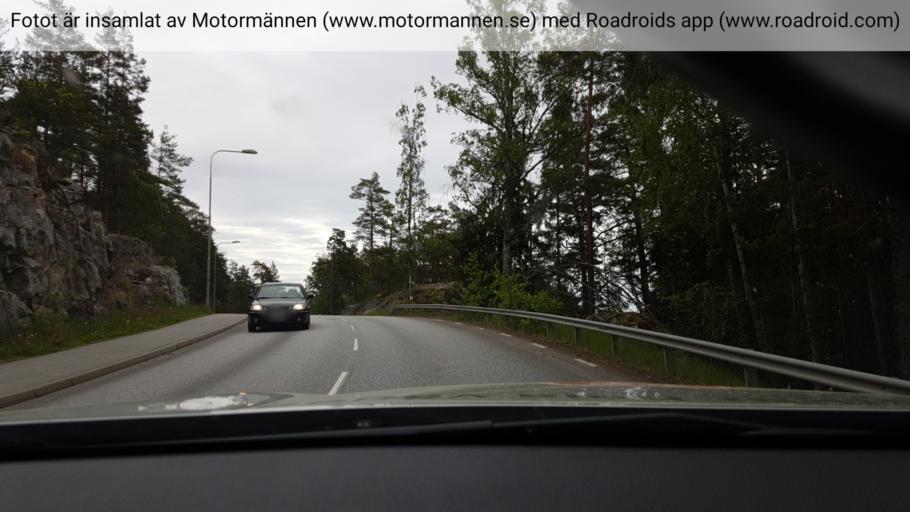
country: SE
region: Stockholm
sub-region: Nacka Kommun
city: Saltsjobaden
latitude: 59.2604
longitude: 18.3202
